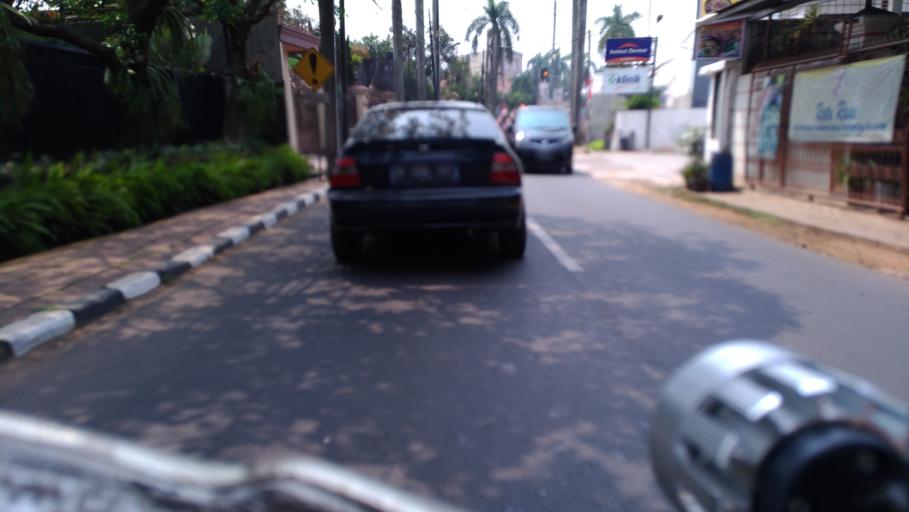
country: ID
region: West Java
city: Cileungsir
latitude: -6.3150
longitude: 106.8994
